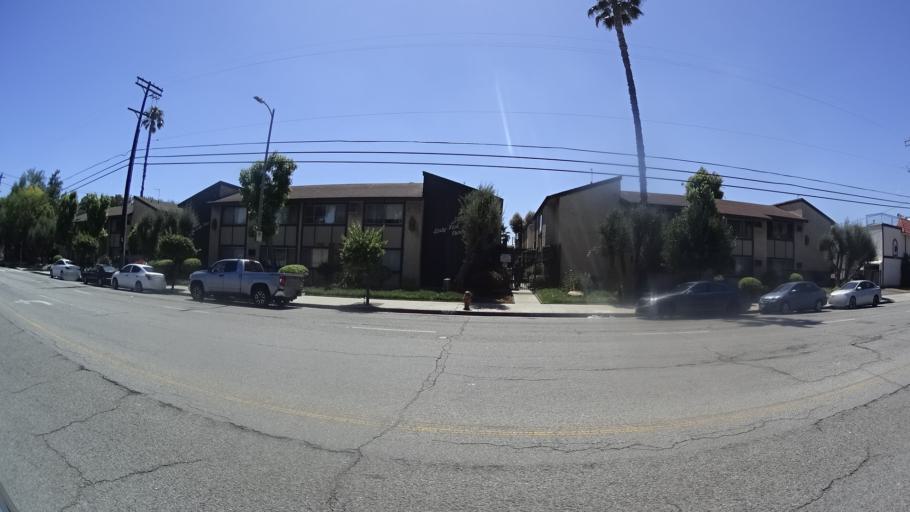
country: US
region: California
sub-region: Los Angeles County
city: Van Nuys
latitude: 34.1902
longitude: -118.4749
